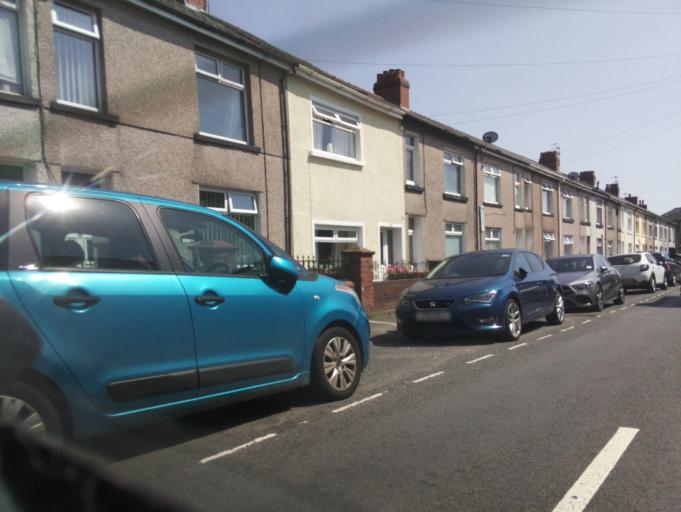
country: GB
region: Wales
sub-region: Caerphilly County Borough
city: Ystrad Mynach
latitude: 51.6406
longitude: -3.2360
